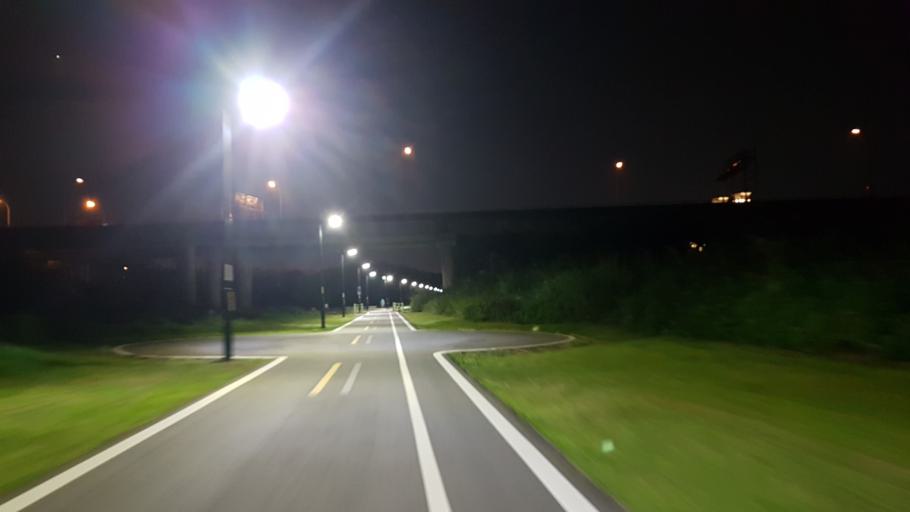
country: TW
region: Taipei
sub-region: Taipei
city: Banqiao
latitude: 24.9694
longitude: 121.5276
